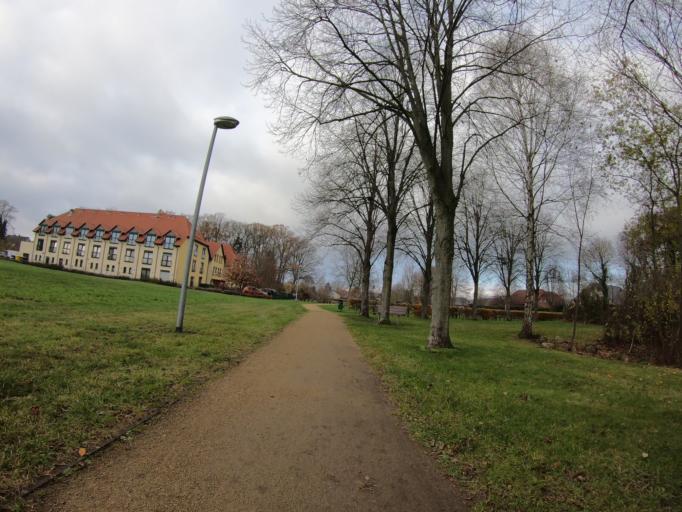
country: DE
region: Lower Saxony
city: Wesendorf
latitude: 52.5880
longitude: 10.5371
